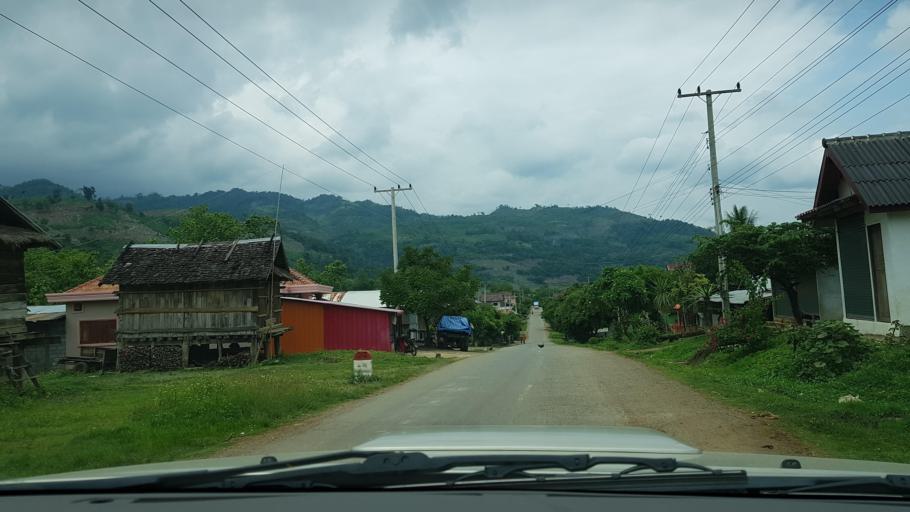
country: TH
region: Nan
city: Chaloem Phra Kiat
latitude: 19.9872
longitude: 101.2766
